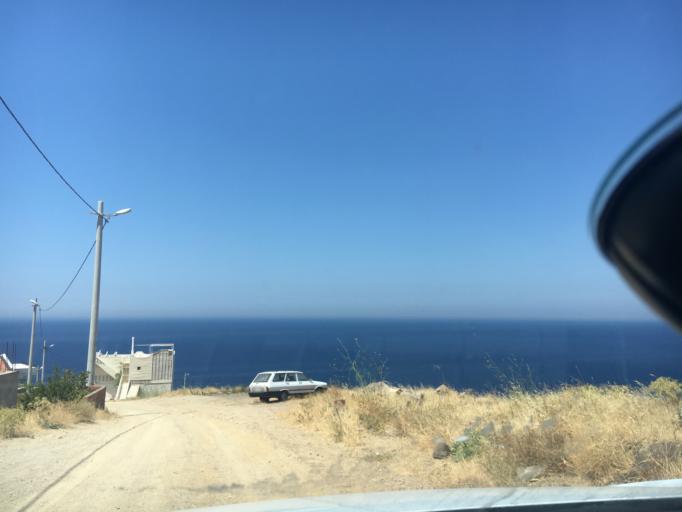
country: TR
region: Canakkale
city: Gulpinar
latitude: 39.4813
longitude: 26.0668
